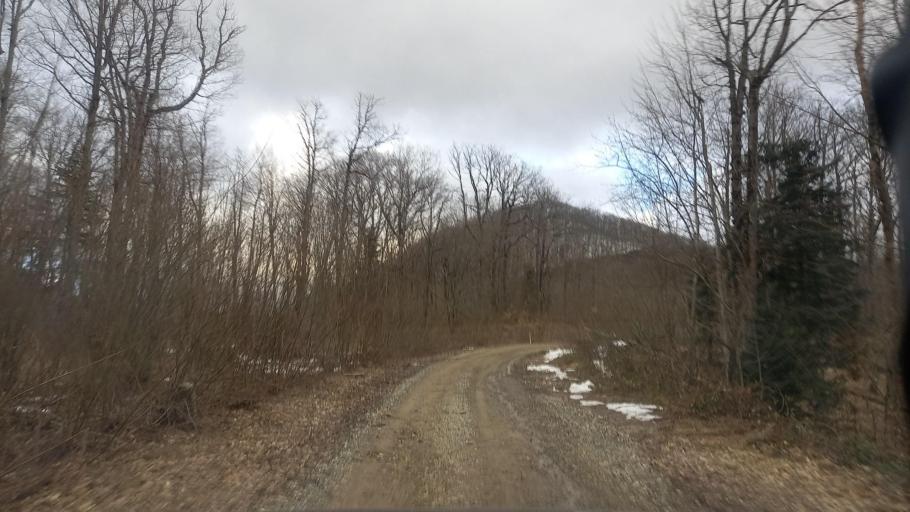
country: RU
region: Krasnodarskiy
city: Dzhubga
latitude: 44.5054
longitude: 38.7817
